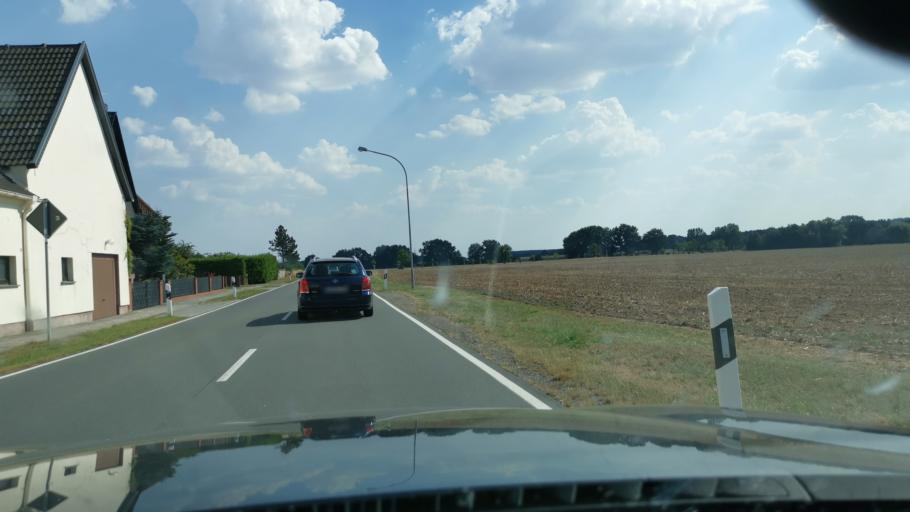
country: DE
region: Saxony
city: Bad Duben
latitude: 51.5584
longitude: 12.5727
